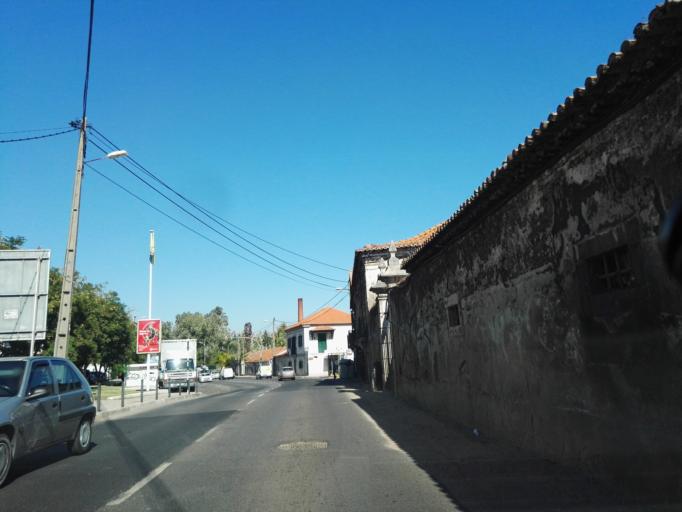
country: PT
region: Lisbon
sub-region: Odivelas
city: Povoa de Santo Adriao
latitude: 38.8095
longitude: -9.1569
